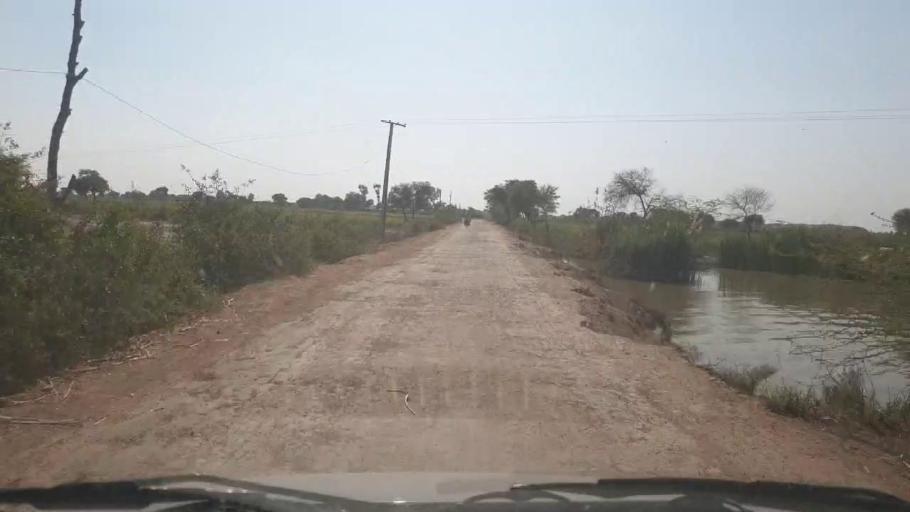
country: PK
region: Sindh
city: Samaro
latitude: 25.2478
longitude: 69.3621
